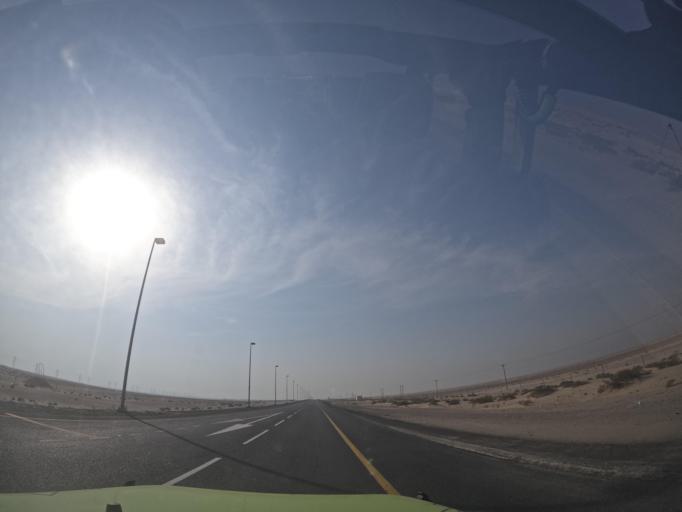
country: AE
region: Dubai
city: Dubai
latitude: 24.7634
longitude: 55.0962
